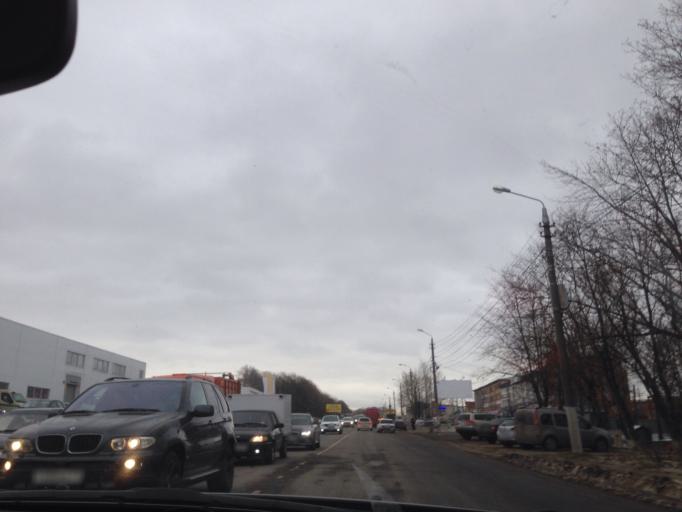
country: RU
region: Tula
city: Tula
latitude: 54.1593
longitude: 37.6370
